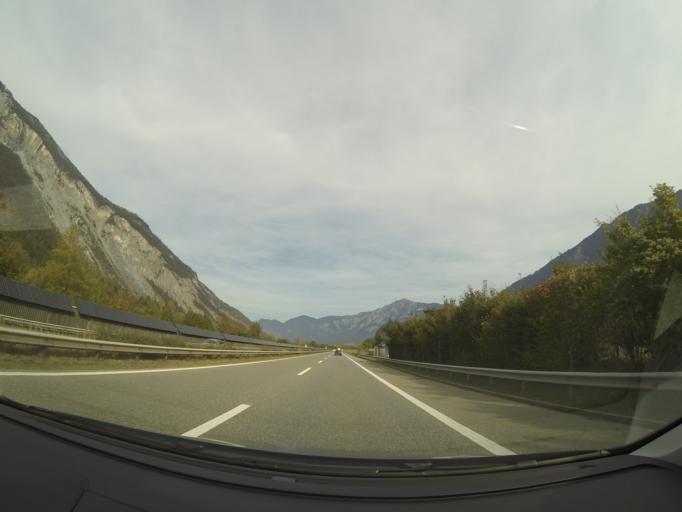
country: CH
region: Grisons
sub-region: Imboden District
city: Domat
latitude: 46.8393
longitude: 9.4633
